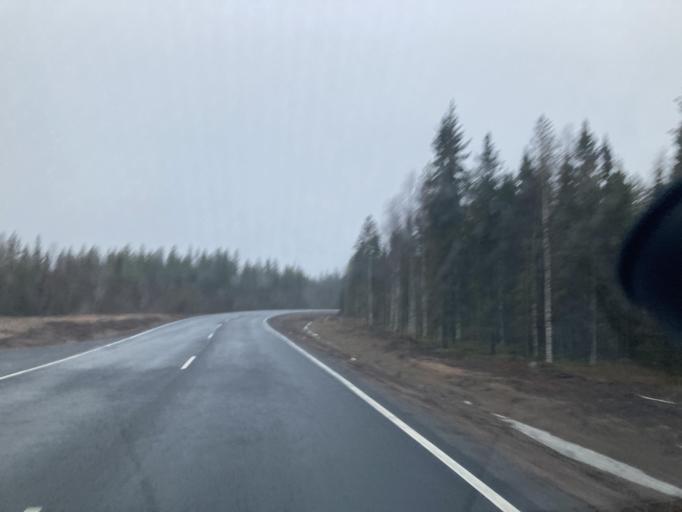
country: FI
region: Lapland
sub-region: Rovaniemi
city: Rovaniemi
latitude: 66.5916
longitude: 25.7950
